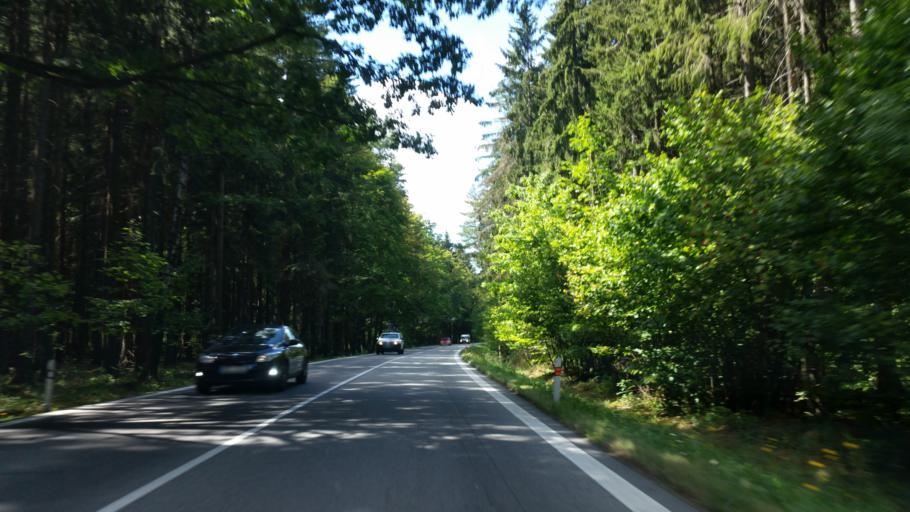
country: CZ
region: Vysocina
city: Cernovice
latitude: 49.4213
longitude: 14.9694
